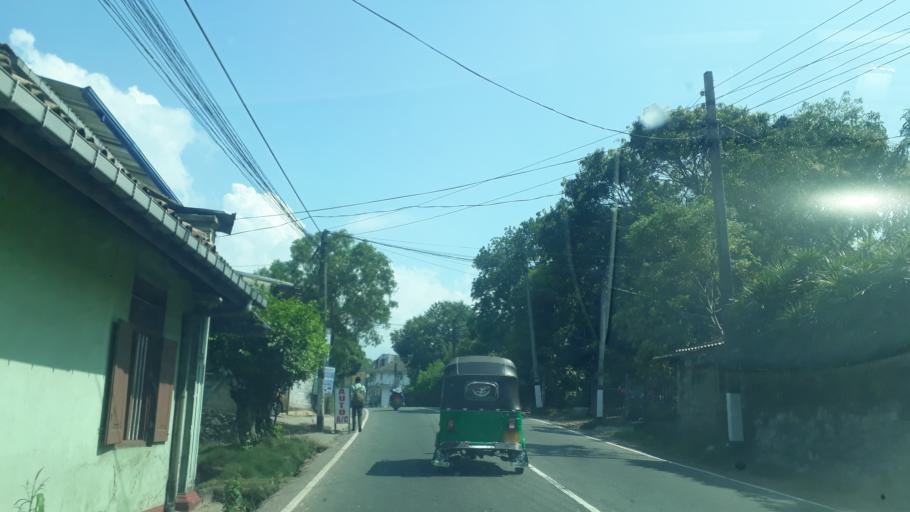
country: LK
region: Western
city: Gampaha
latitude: 7.0756
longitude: 80.0143
